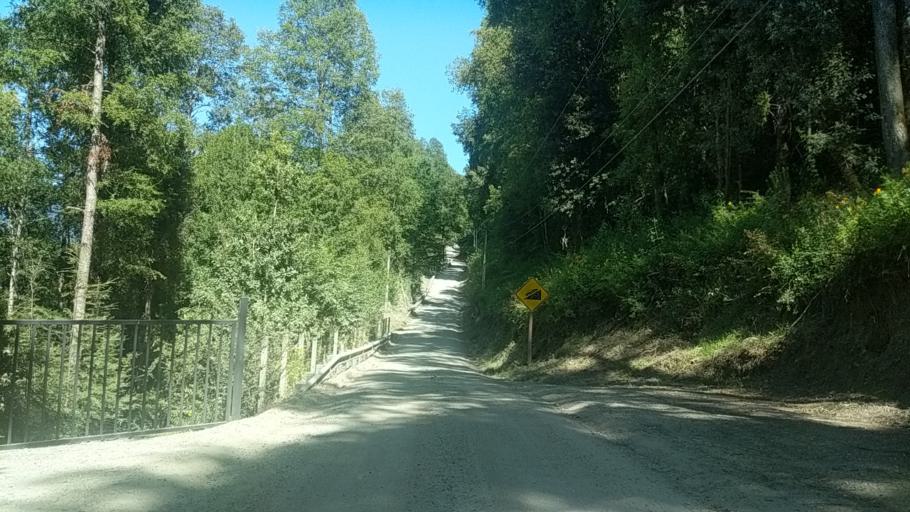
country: CL
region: Araucania
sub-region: Provincia de Cautin
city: Pucon
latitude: -39.0634
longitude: -71.7206
